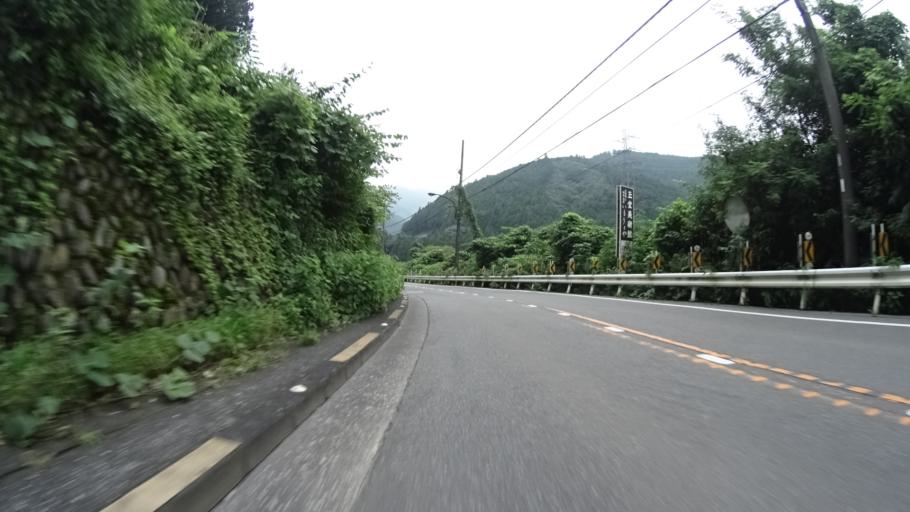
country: JP
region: Tokyo
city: Ome
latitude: 35.8040
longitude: 139.1882
